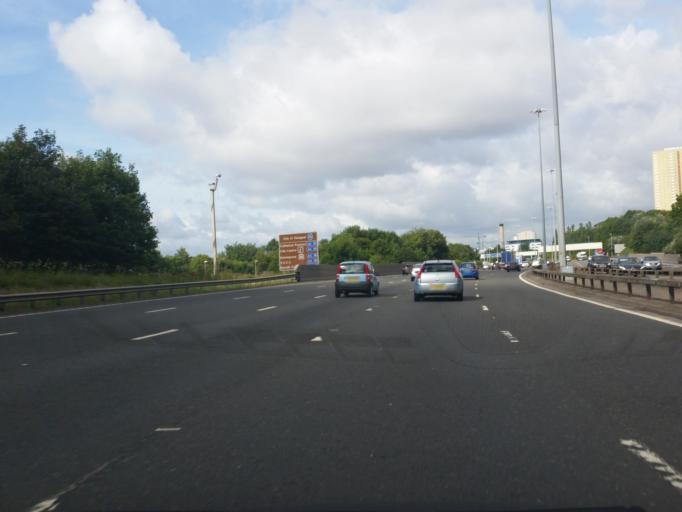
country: GB
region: Scotland
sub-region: South Lanarkshire
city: Rutherglen
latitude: 55.8671
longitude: -4.2128
